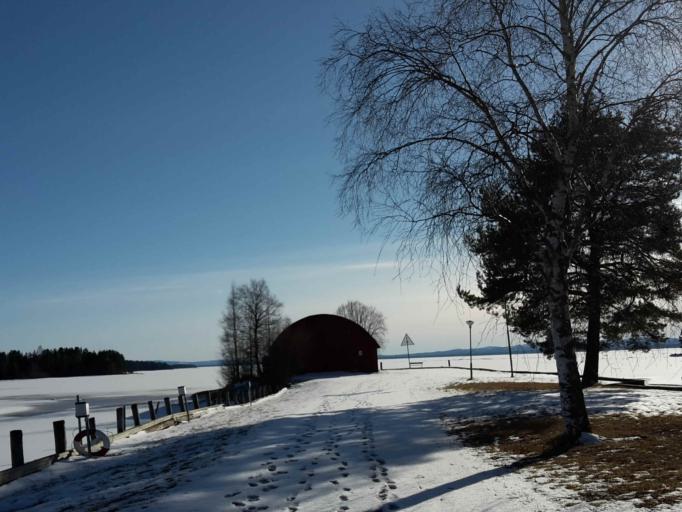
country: SE
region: Dalarna
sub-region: Orsa Kommun
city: Orsa
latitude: 61.1171
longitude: 14.6067
